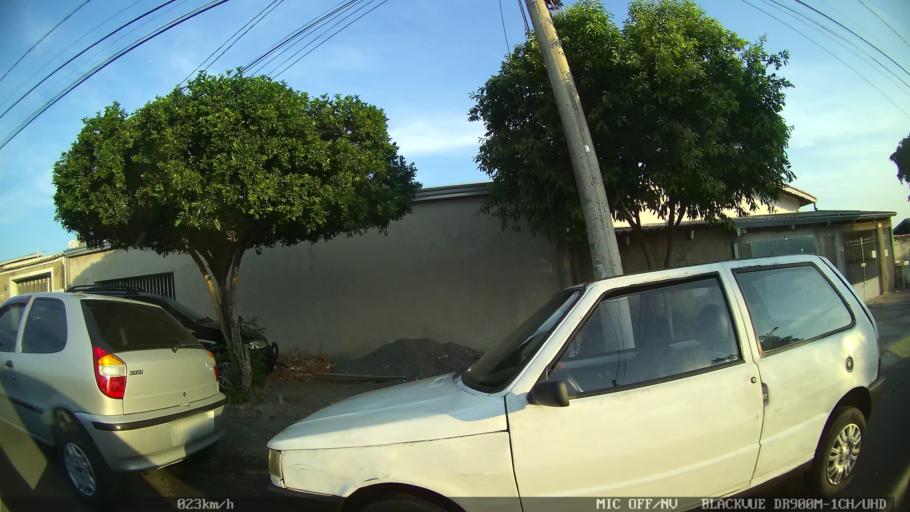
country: BR
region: Sao Paulo
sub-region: Campinas
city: Campinas
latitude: -22.9698
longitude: -47.1296
